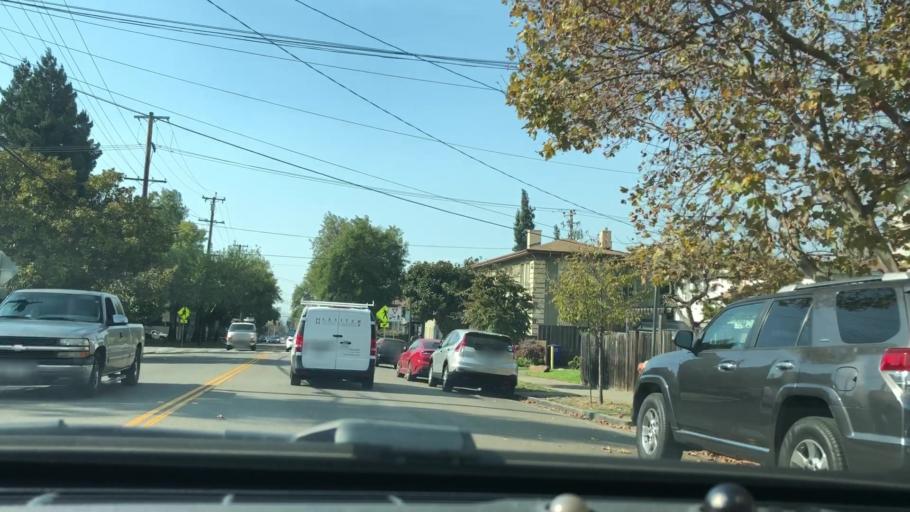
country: US
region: California
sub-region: Alameda County
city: Berkeley
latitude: 37.8567
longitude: -122.2561
